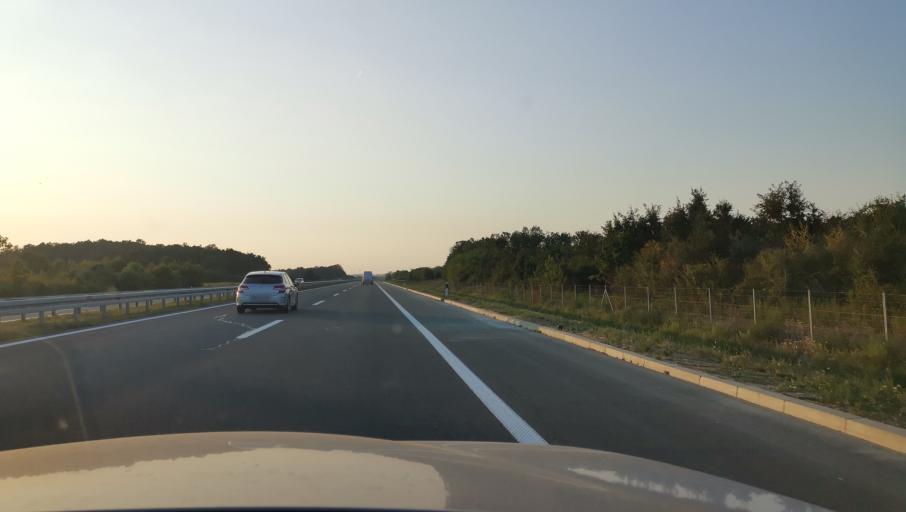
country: RS
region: Central Serbia
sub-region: Kolubarski Okrug
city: Lajkovac
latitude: 44.3854
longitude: 20.1096
